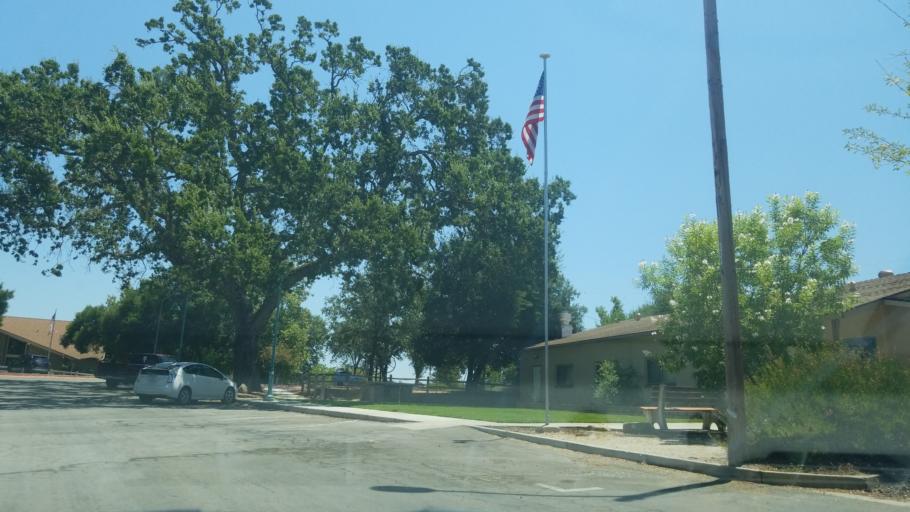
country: US
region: California
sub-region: San Luis Obispo County
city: Atascadero
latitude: 35.4661
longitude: -120.6694
